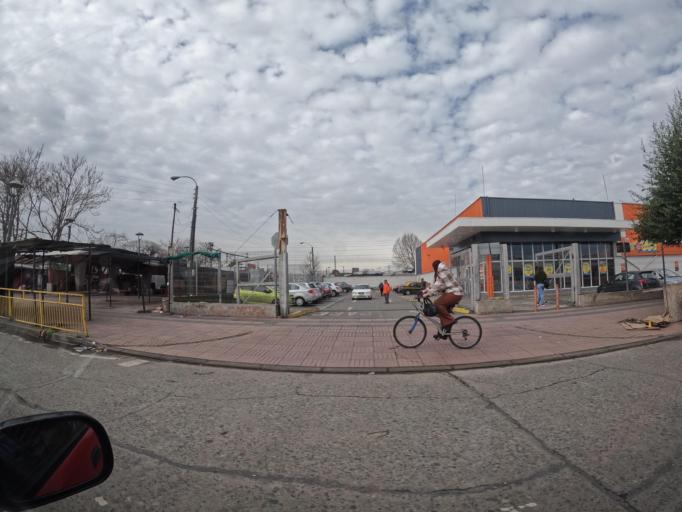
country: CL
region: Maule
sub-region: Provincia de Linares
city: Linares
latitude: -35.8456
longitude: -71.5907
